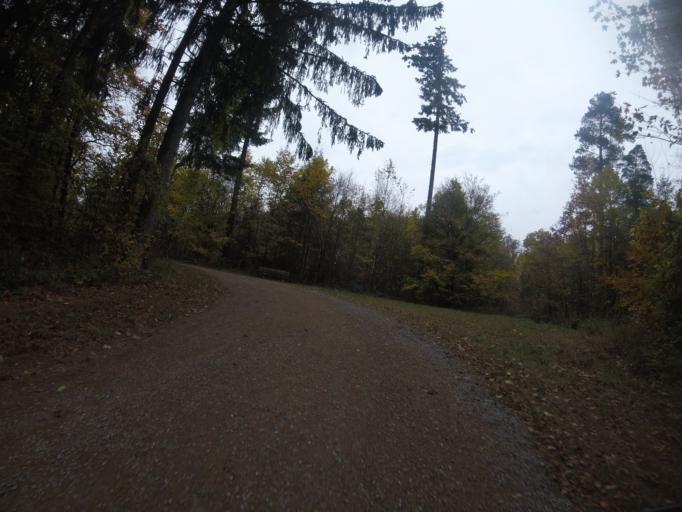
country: DE
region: Baden-Wuerttemberg
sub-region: Regierungsbezirk Stuttgart
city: Grossbottwar
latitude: 48.9807
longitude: 9.3261
